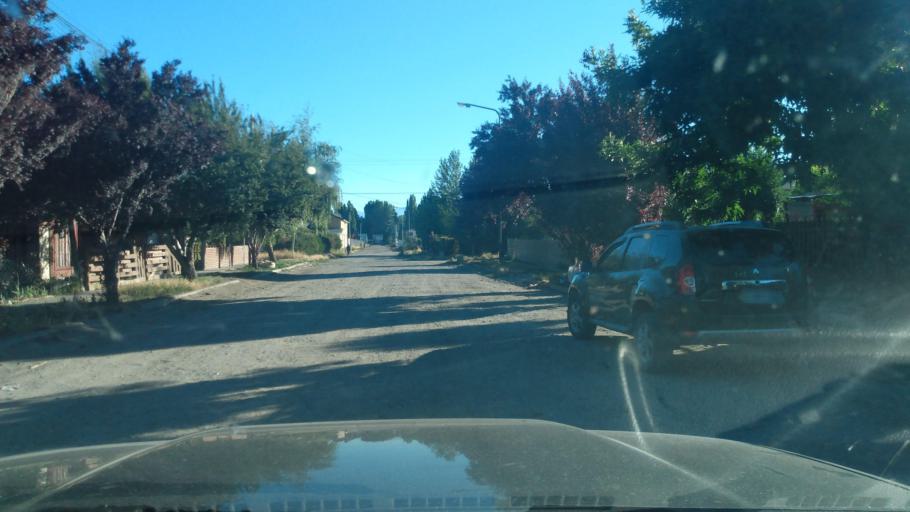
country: AR
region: Neuquen
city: Junin de los Andes
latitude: -39.9536
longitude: -71.0785
